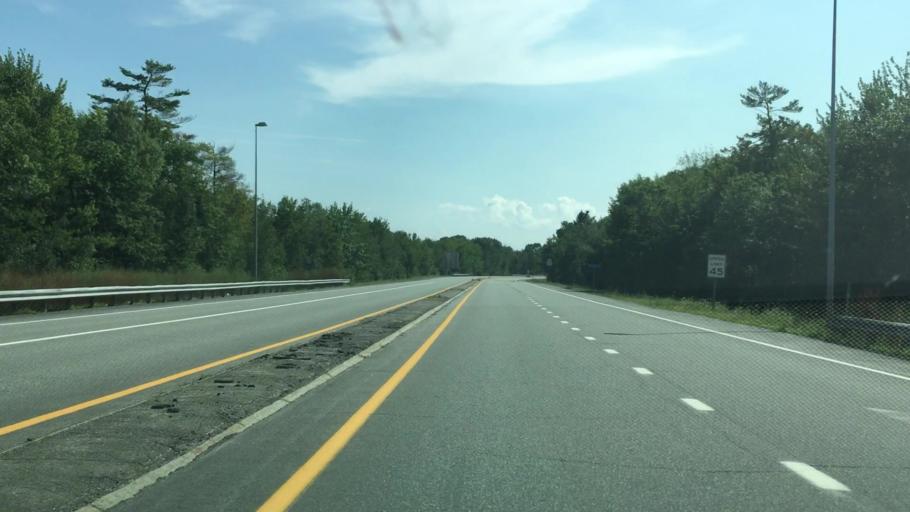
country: US
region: Maine
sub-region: Penobscot County
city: Bangor
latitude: 44.7840
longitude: -68.7949
